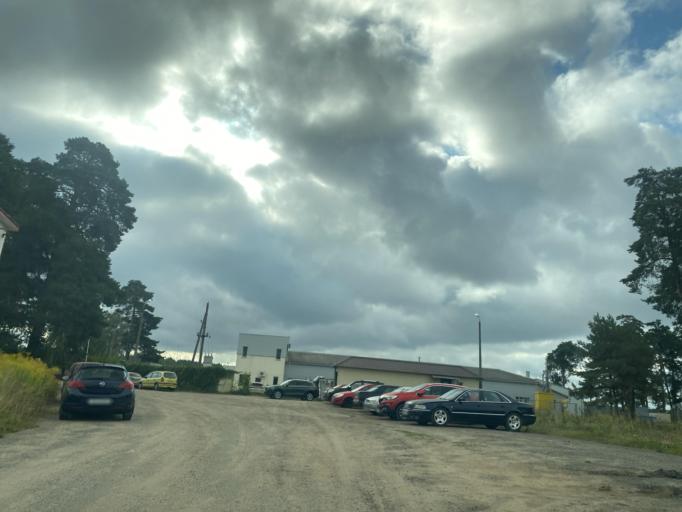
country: BY
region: Minsk
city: Bal'shavik
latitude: 53.9874
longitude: 27.5877
